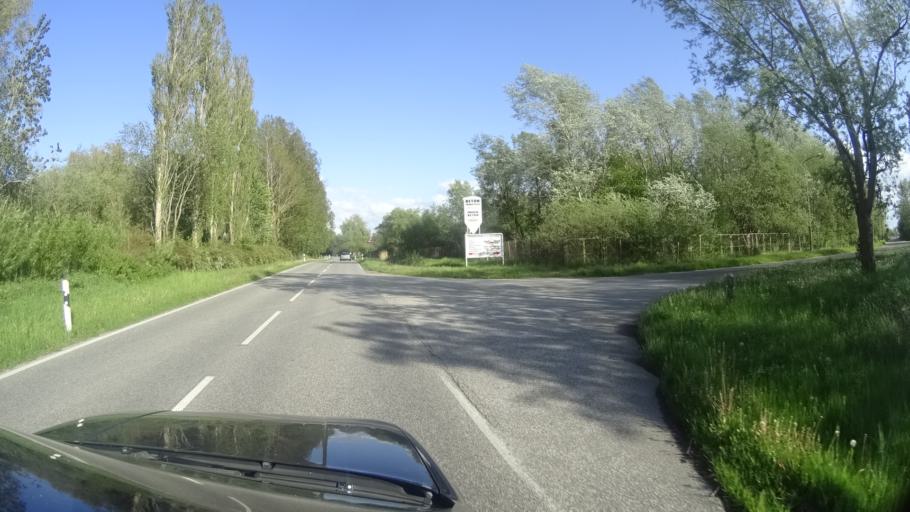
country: DE
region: Mecklenburg-Vorpommern
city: Ostseebad Dierhagen
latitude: 54.2502
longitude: 12.3949
